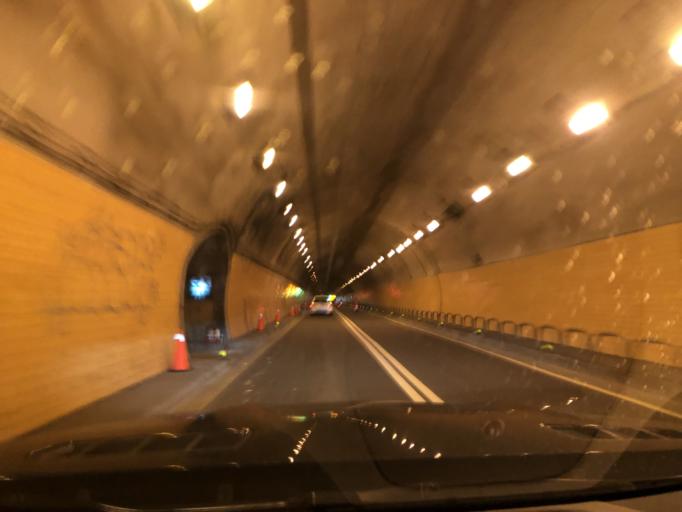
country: TW
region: Taipei
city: Taipei
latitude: 24.9954
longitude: 121.5517
